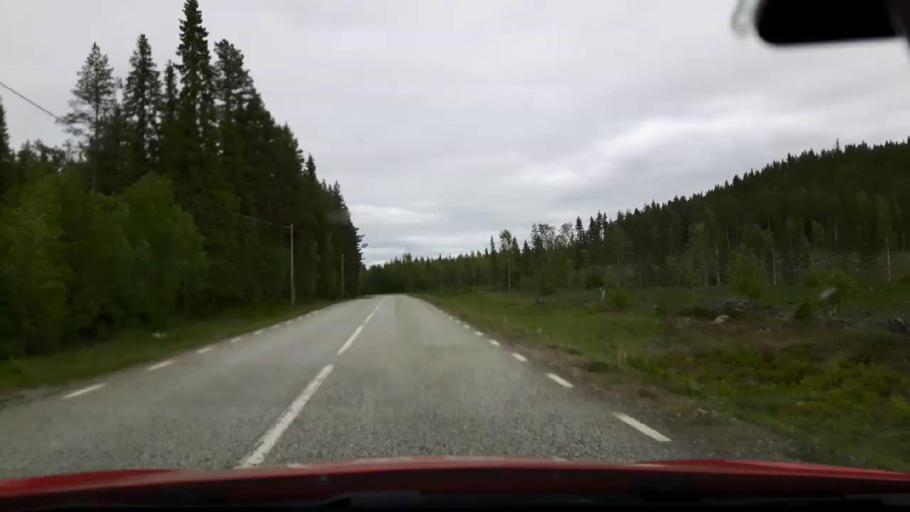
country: SE
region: Jaemtland
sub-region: Stroemsunds Kommun
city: Stroemsund
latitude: 63.3518
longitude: 15.7230
